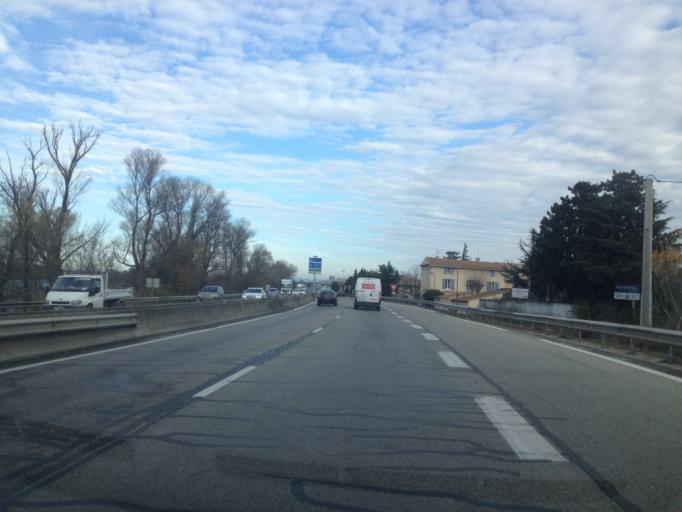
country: FR
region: Provence-Alpes-Cote d'Azur
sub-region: Departement du Vaucluse
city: Le Pontet
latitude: 43.9652
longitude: 4.8532
